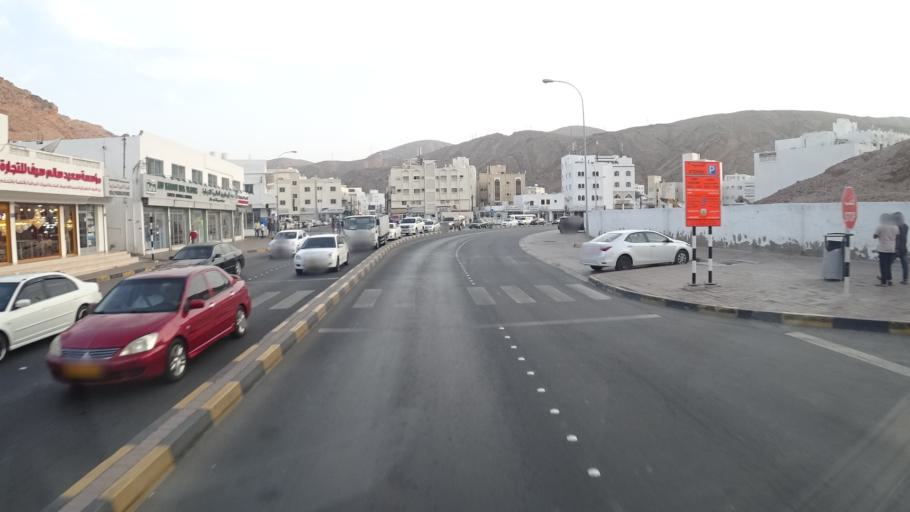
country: OM
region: Muhafazat Masqat
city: Muscat
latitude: 23.5835
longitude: 58.5455
